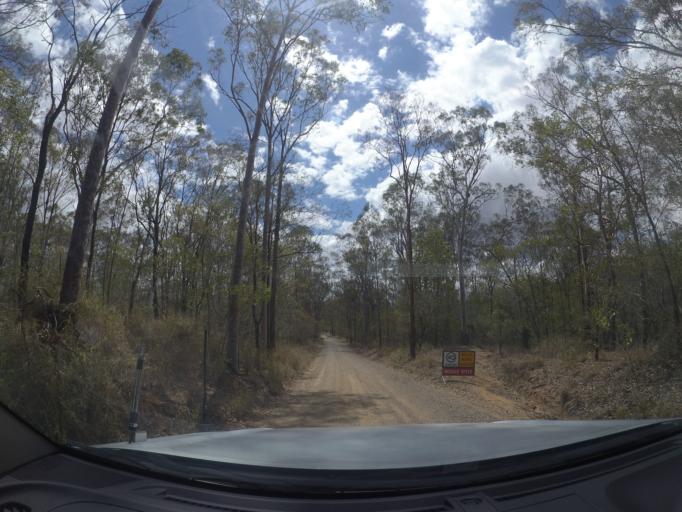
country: AU
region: Queensland
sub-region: Logan
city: Cedar Vale
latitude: -27.8891
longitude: 153.0434
